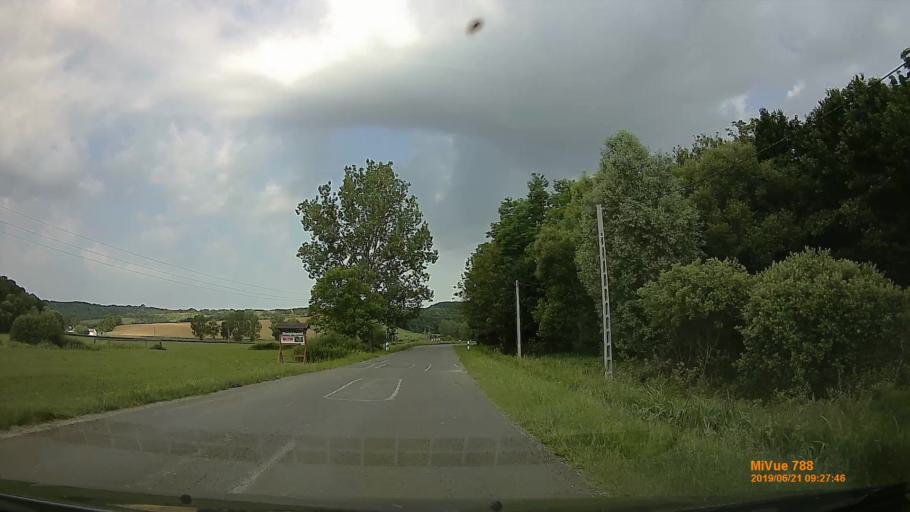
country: HU
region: Somogy
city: Taszar
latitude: 46.2789
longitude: 17.8940
